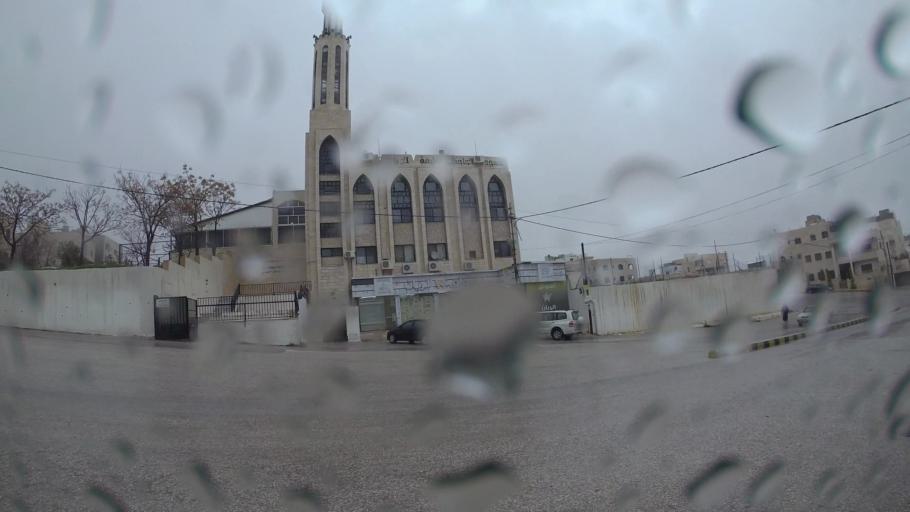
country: JO
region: Amman
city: Al Jubayhah
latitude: 32.0490
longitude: 35.8783
